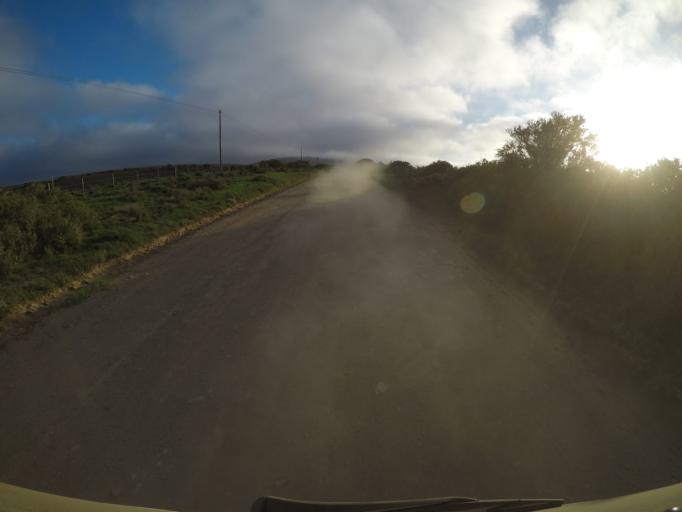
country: ZA
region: Western Cape
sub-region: Eden District Municipality
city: Mossel Bay
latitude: -34.1323
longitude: 22.0452
